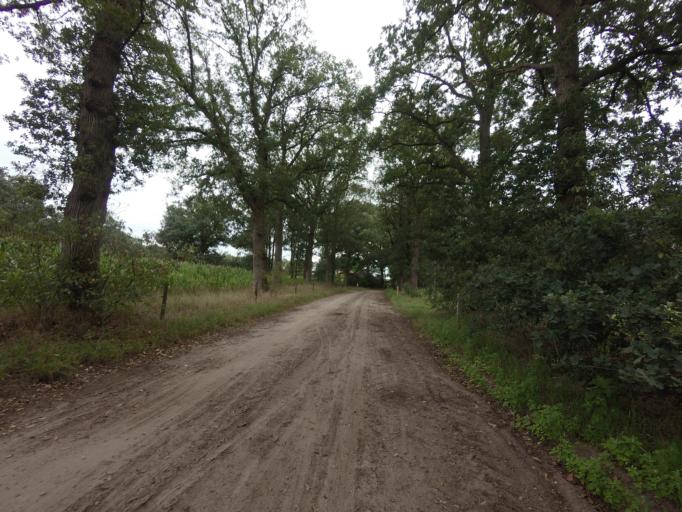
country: NL
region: Gelderland
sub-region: Gemeente Lochem
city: Laren
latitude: 52.2874
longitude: 6.4013
